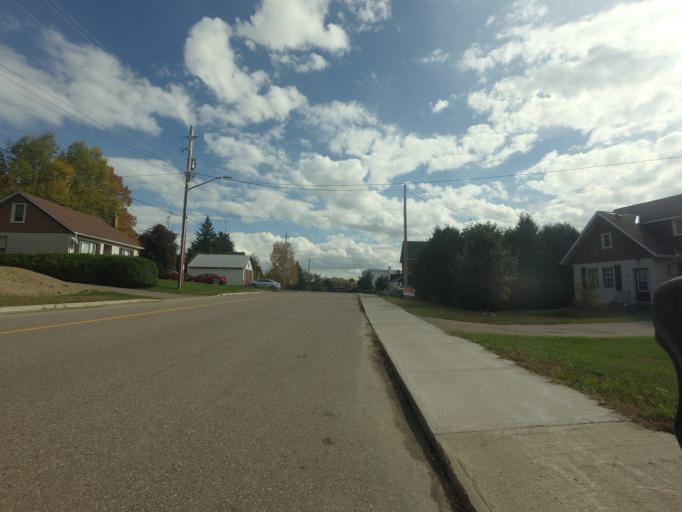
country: CA
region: Ontario
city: Pembroke
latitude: 45.5418
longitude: -77.1042
